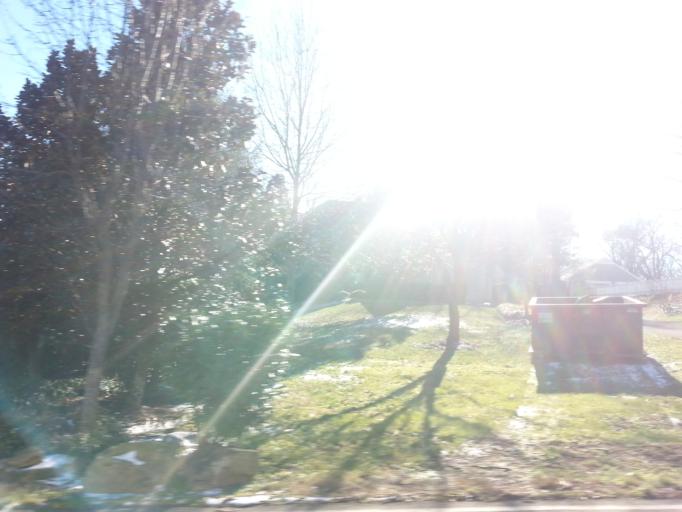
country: US
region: Tennessee
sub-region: Knox County
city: Knoxville
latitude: 35.9226
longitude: -84.0006
